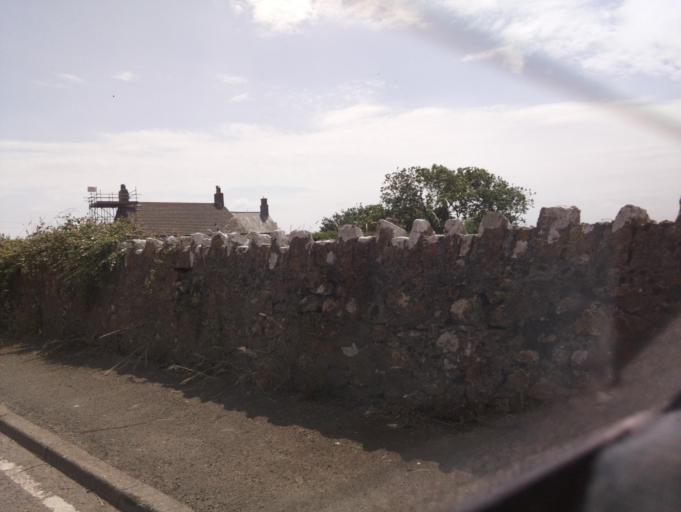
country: GB
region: Wales
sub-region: Bridgend county borough
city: Merthyr Mawr
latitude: 51.4548
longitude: -3.5873
